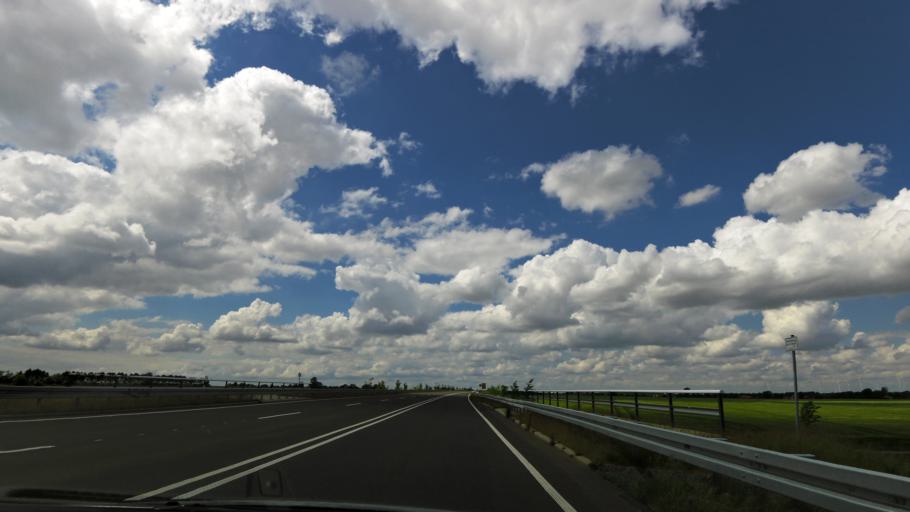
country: DE
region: North Rhine-Westphalia
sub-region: Regierungsbezirk Koln
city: Gangelt
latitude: 51.0101
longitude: 6.0240
